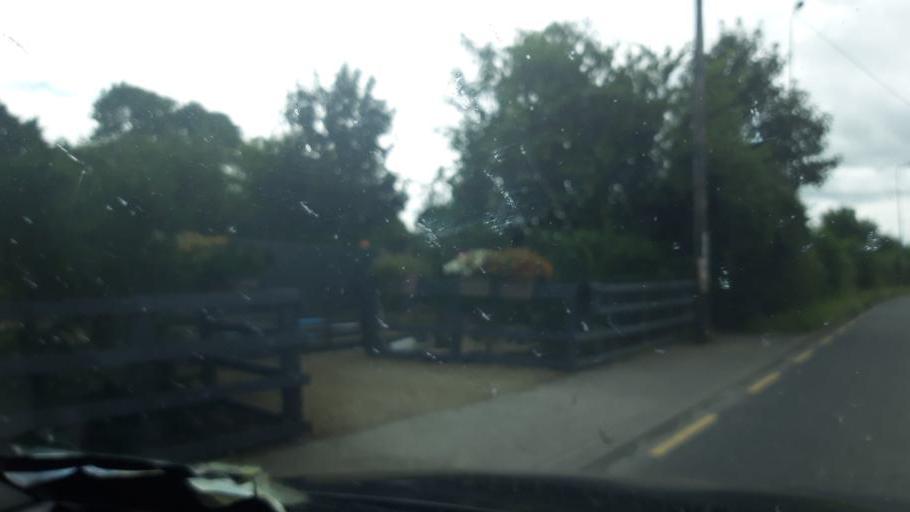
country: IE
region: Leinster
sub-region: Kilkenny
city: Callan
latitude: 52.4608
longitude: -7.4633
